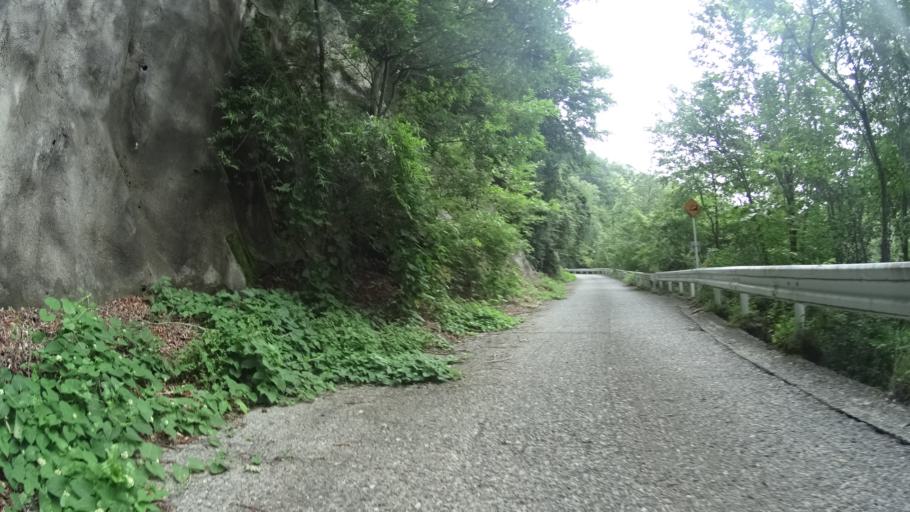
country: JP
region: Yamanashi
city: Kofu-shi
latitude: 35.8484
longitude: 138.5772
